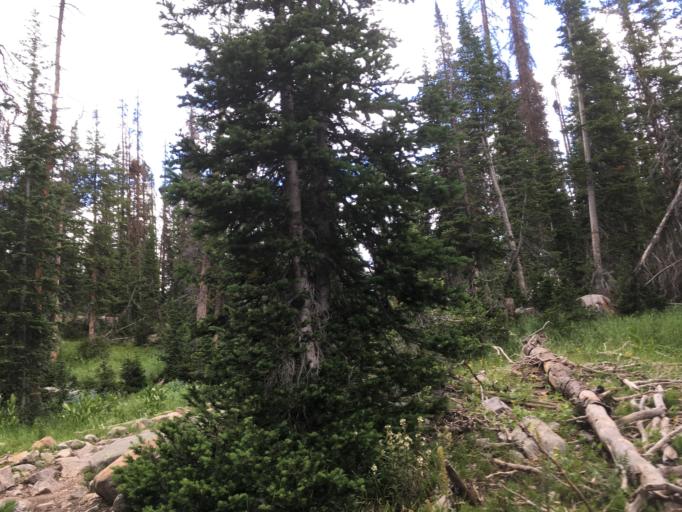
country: US
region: Utah
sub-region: Summit County
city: Kamas
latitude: 40.7176
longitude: -110.8824
